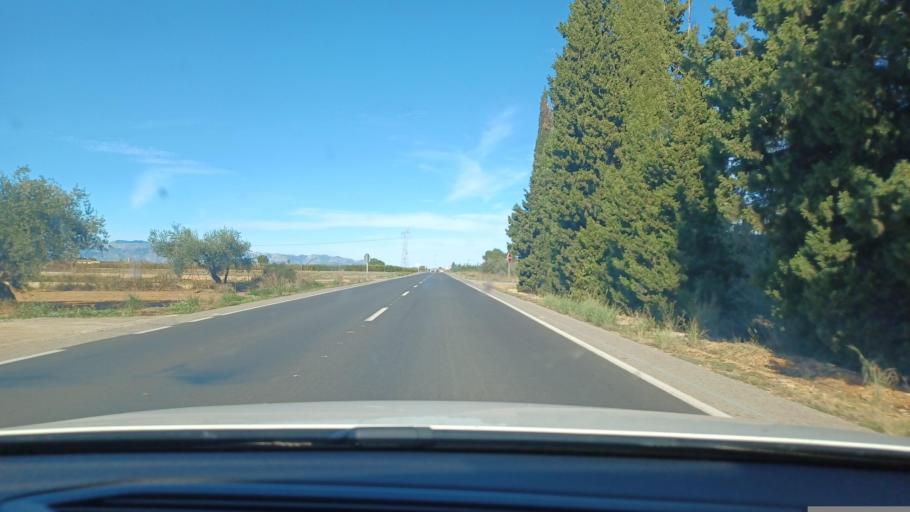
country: ES
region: Catalonia
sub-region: Provincia de Tarragona
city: Santa Barbara
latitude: 40.7017
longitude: 0.5042
